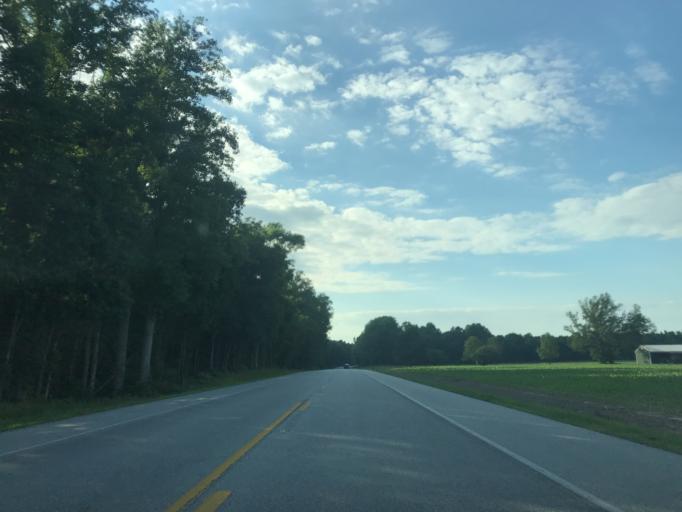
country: US
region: Maryland
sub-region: Caroline County
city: Federalsburg
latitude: 38.7324
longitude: -75.7884
